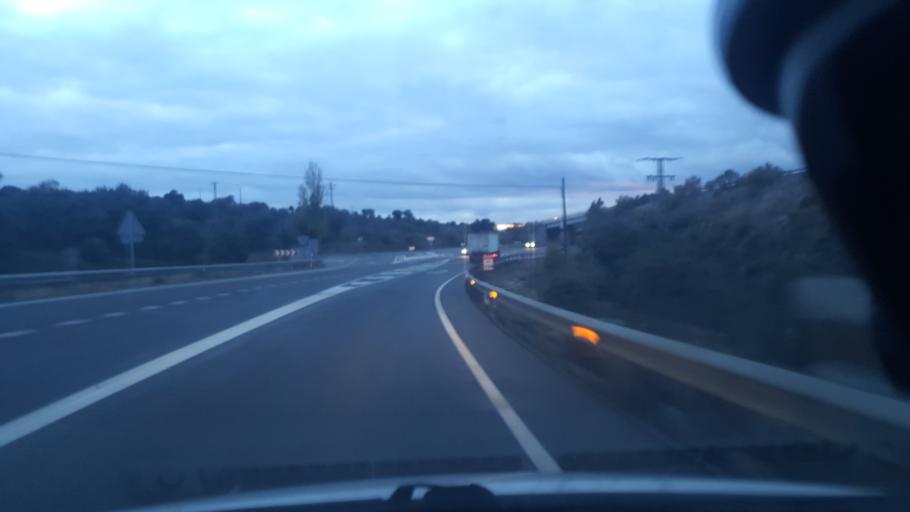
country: ES
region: Castille and Leon
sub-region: Provincia de Avila
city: Ojos-Albos
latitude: 40.7194
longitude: -4.5324
